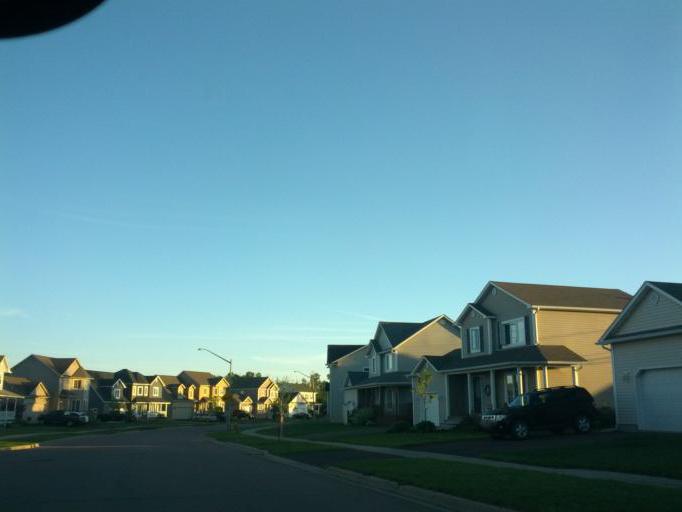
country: CA
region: New Brunswick
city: Moncton
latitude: 46.1126
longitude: -64.8621
